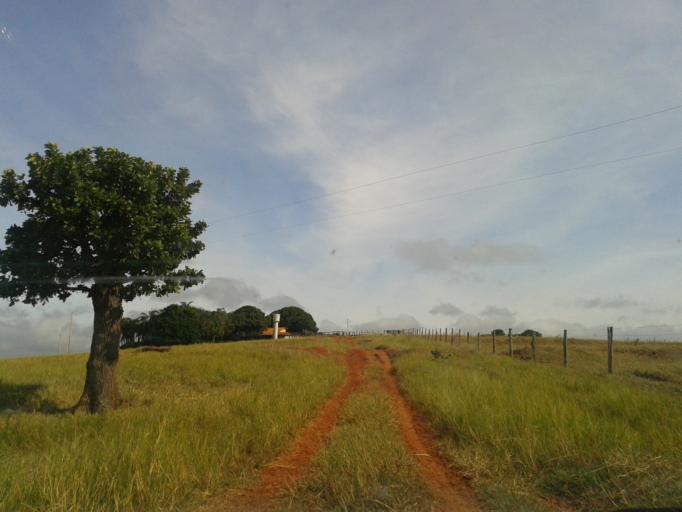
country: BR
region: Minas Gerais
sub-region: Campina Verde
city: Campina Verde
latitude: -19.4124
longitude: -49.6598
